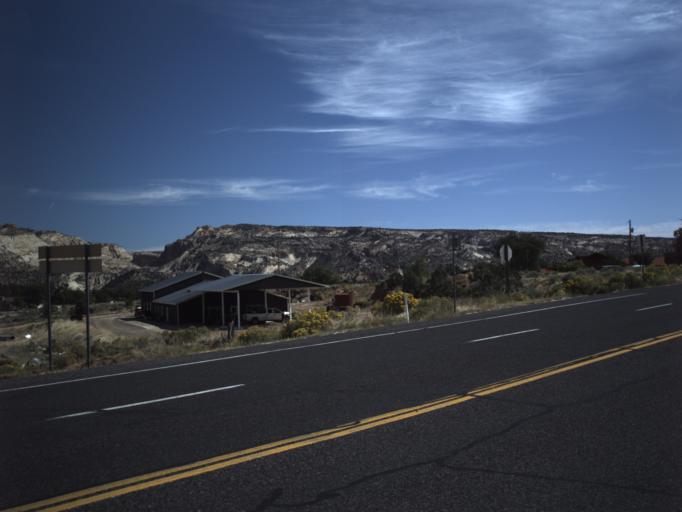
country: US
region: Utah
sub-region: Wayne County
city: Loa
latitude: 37.7719
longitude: -111.6123
